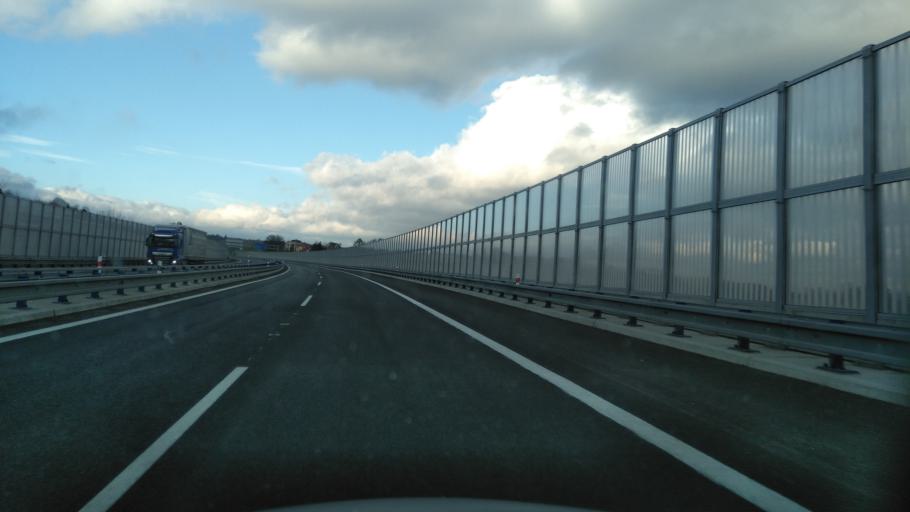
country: CZ
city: Bystrice
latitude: 49.6420
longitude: 18.7029
